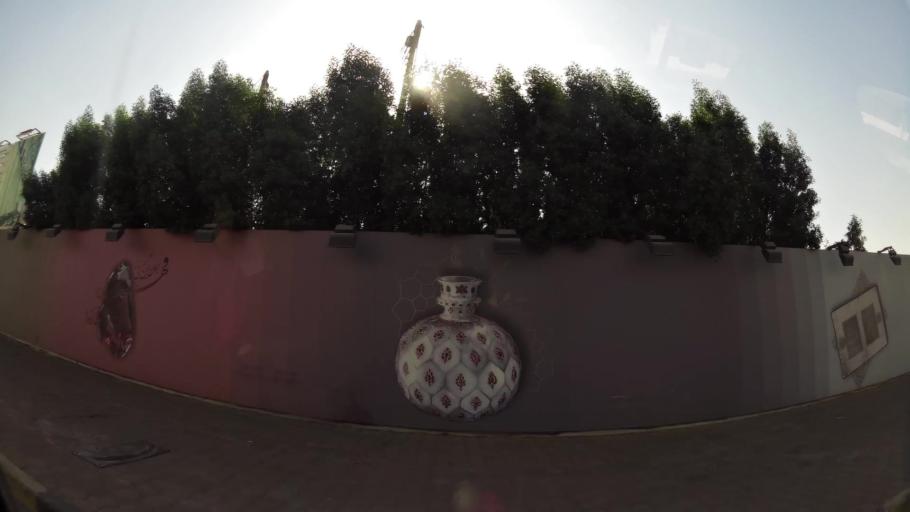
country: KW
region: Al Asimah
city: Kuwait City
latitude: 29.3745
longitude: 47.9668
